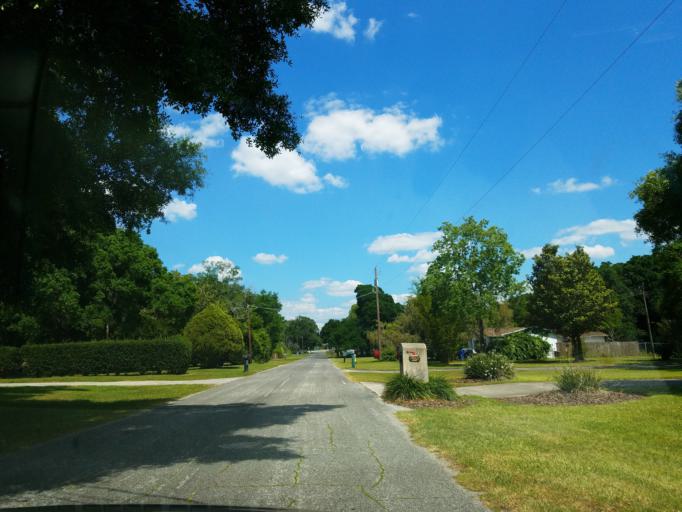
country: US
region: Florida
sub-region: Hillsborough County
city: Brandon
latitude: 27.9159
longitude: -82.2667
